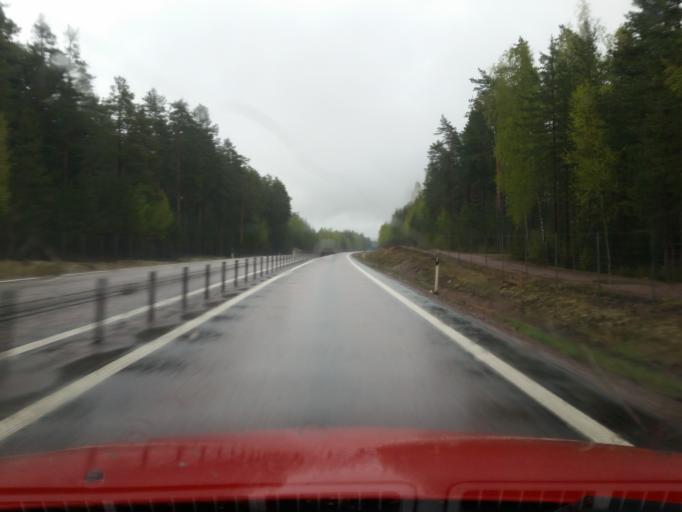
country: SE
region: Dalarna
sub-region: Saters Kommun
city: Saeter
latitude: 60.3867
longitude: 15.6489
